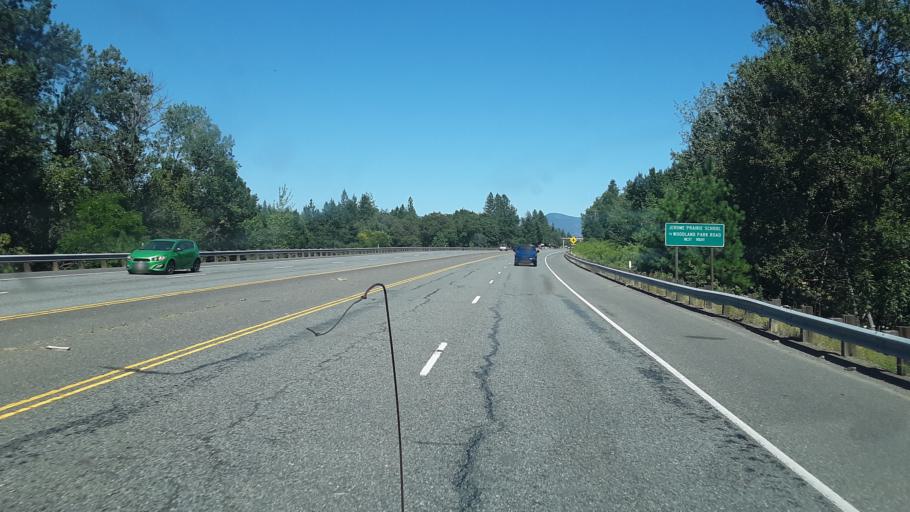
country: US
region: Oregon
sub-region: Josephine County
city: Redwood
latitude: 42.4097
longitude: -123.4314
